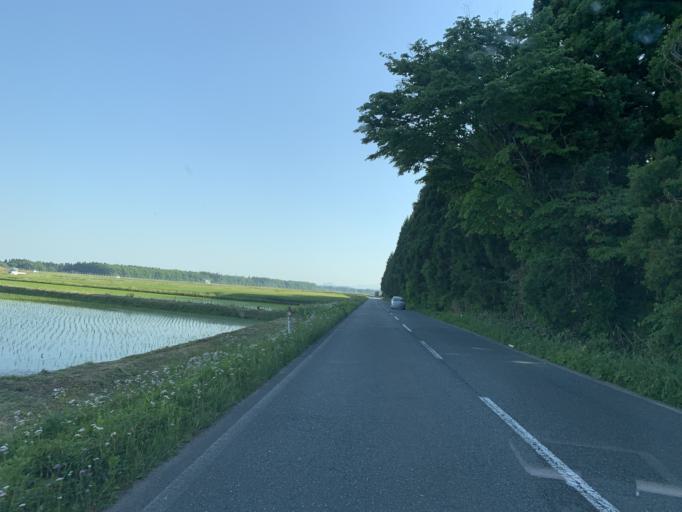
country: JP
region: Iwate
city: Kitakami
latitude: 39.2715
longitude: 141.0470
